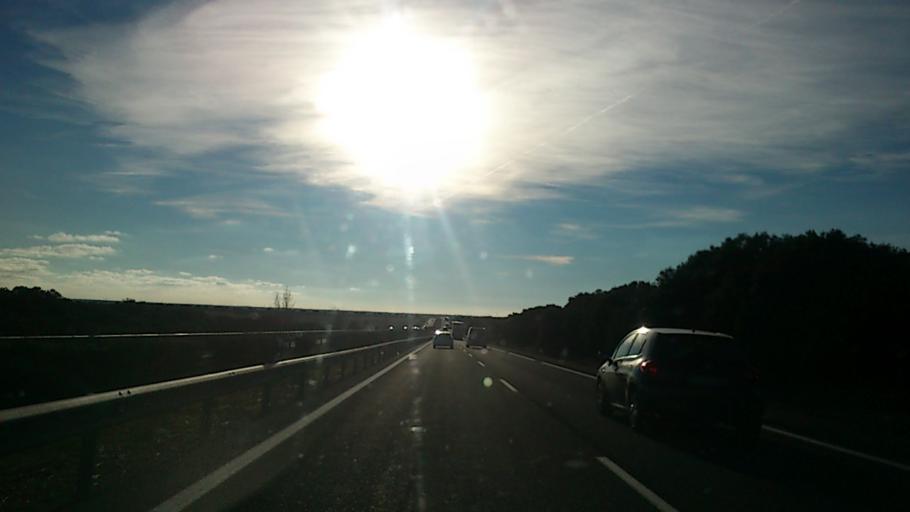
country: ES
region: Castille-La Mancha
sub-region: Provincia de Guadalajara
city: Algora
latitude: 40.9489
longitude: -2.6884
